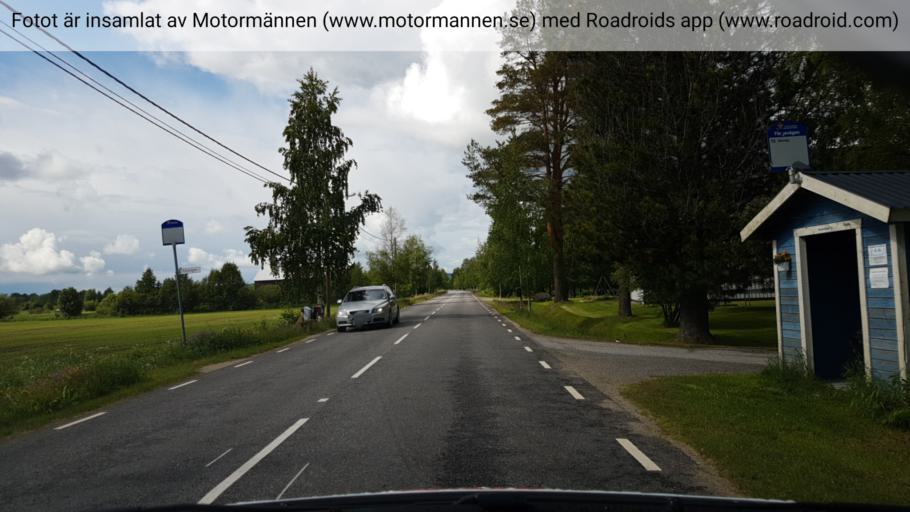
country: SE
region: Vaesterbotten
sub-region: Vannas Kommun
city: Vannasby
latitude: 63.9009
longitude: 19.8709
